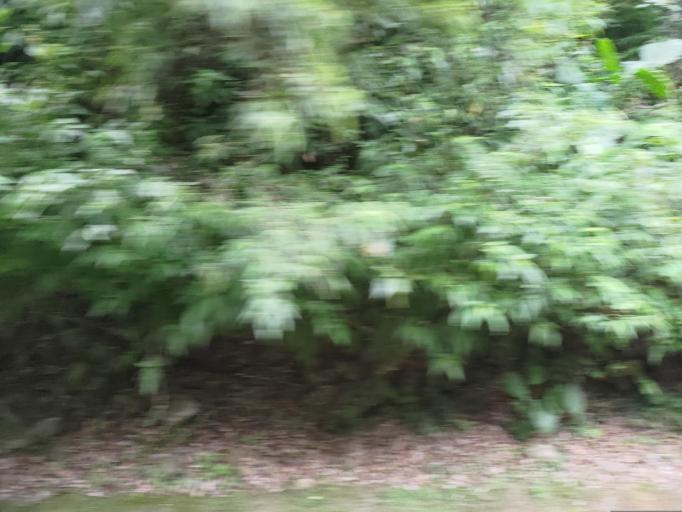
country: TW
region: Taiwan
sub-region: Hsinchu
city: Hsinchu
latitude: 24.6036
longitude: 121.0382
